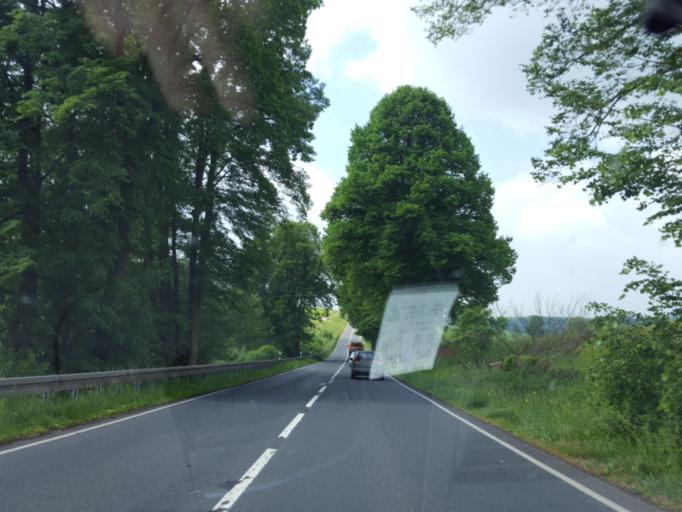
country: DE
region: Lower Saxony
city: Wulften
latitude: 51.7081
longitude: 10.1671
